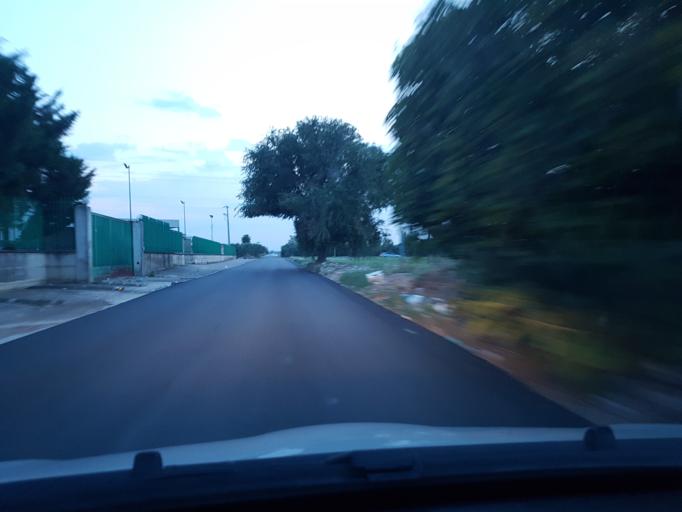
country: IT
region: Apulia
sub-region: Provincia di Foggia
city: Cerignola
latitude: 41.2596
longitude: 15.8824
